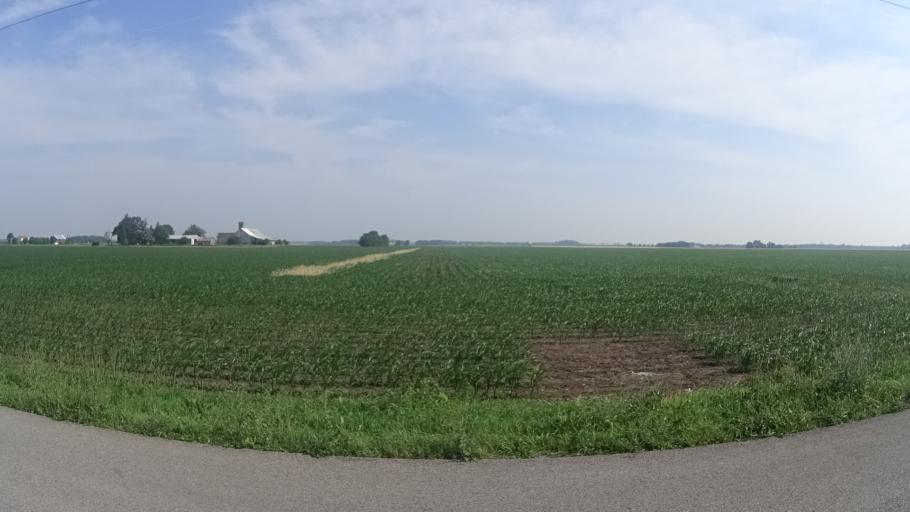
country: US
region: Ohio
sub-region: Huron County
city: Bellevue
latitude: 41.2982
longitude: -82.8017
